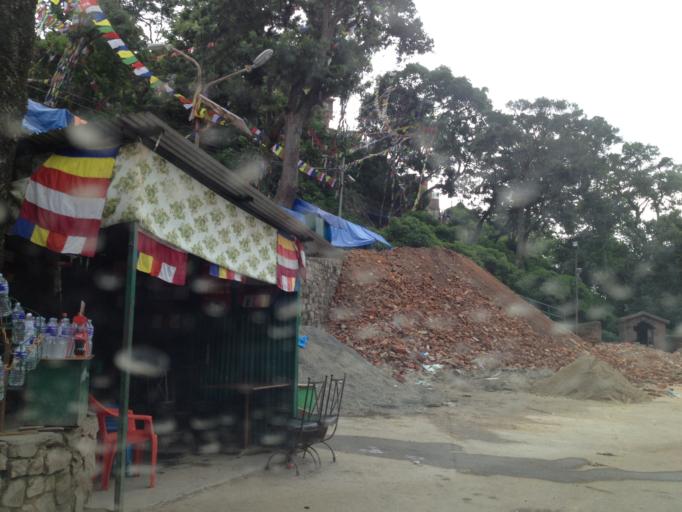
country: NP
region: Central Region
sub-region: Bagmati Zone
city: Kathmandu
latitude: 27.7157
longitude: 85.2893
